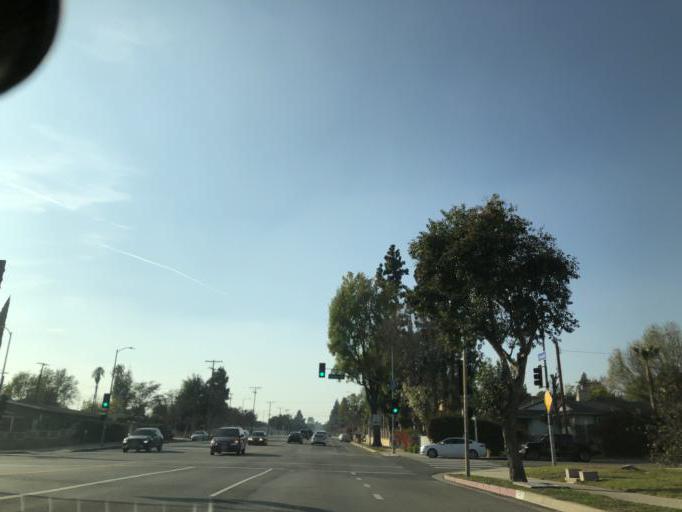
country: US
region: California
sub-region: Los Angeles County
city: Northridge
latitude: 34.2795
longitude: -118.5105
